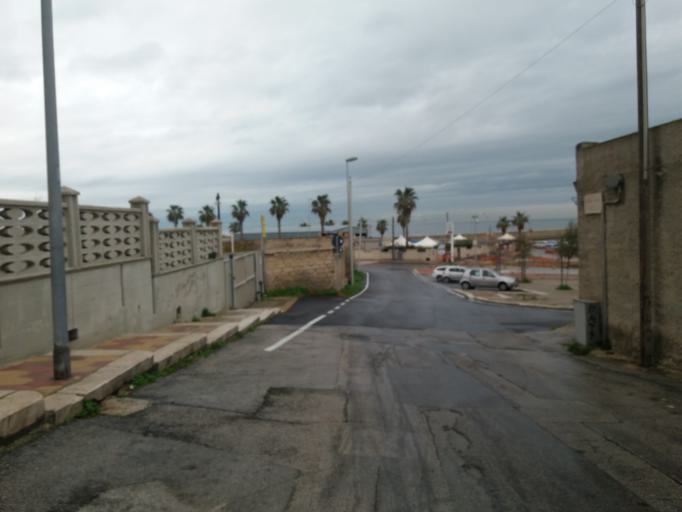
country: IT
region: Apulia
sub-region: Provincia di Bari
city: San Paolo
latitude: 41.1393
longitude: 16.8097
